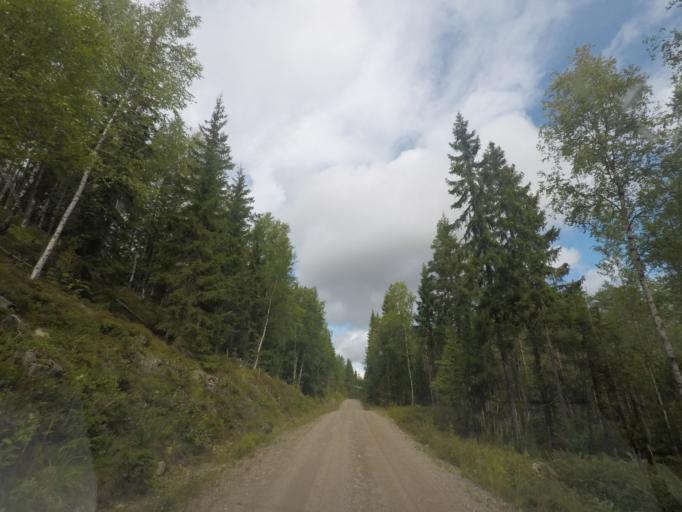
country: SE
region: Vaermland
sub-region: Filipstads Kommun
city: Lesjofors
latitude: 60.0649
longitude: 14.4356
